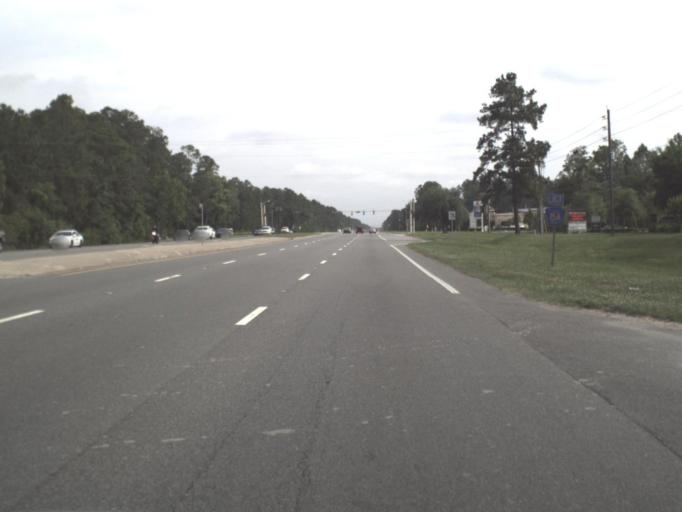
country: US
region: Florida
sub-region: Saint Johns County
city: Fruit Cove
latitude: 30.0662
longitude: -81.7073
